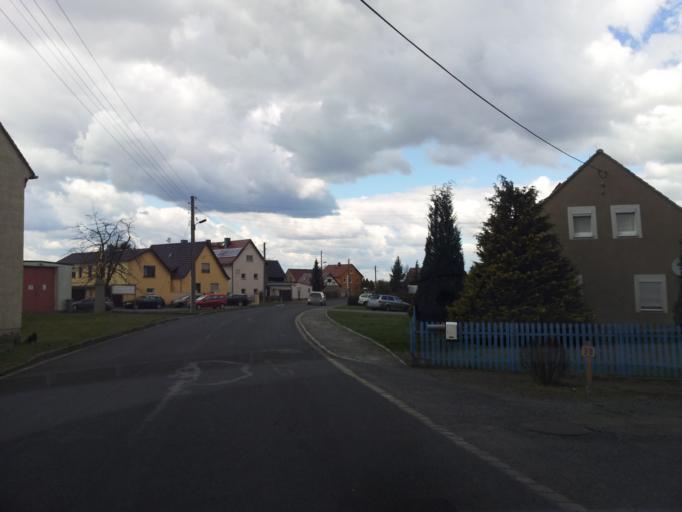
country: DE
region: Saxony
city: Horka
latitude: 51.2894
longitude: 14.2274
